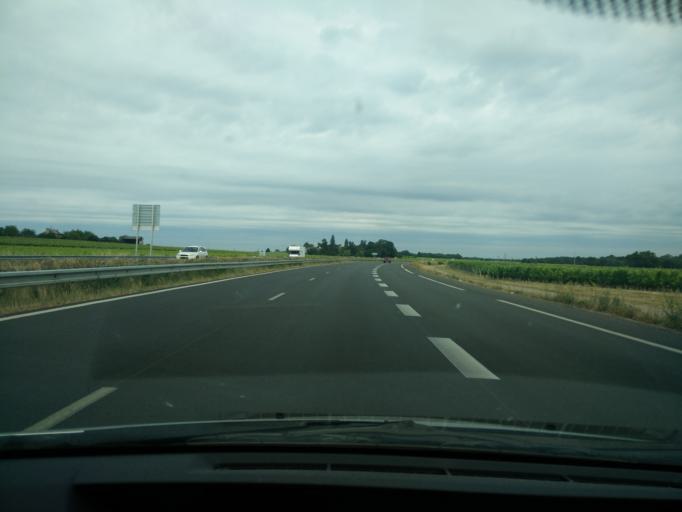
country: FR
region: Pays de la Loire
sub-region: Departement de Maine-et-Loire
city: Brissac-Quince
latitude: 47.3742
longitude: -0.4672
